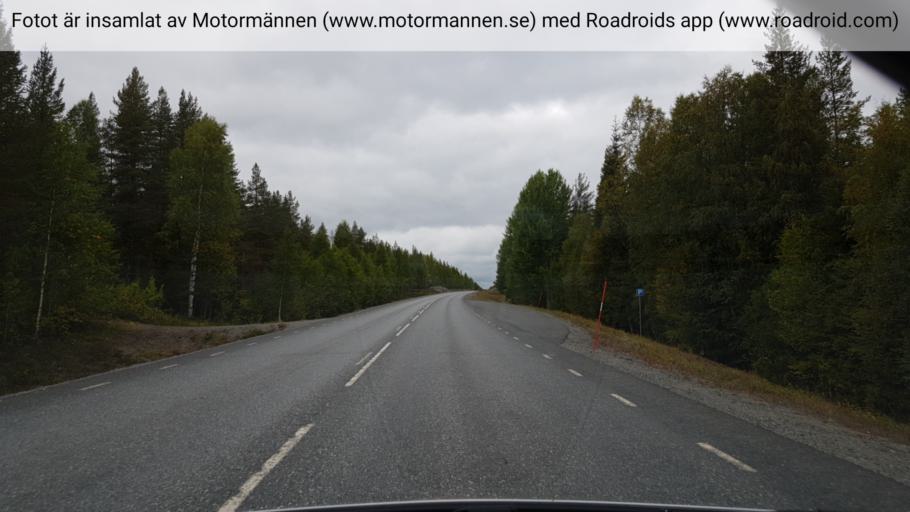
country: SE
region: Vaesterbotten
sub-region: Skelleftea Kommun
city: Langsele
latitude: 64.8863
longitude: 20.1940
